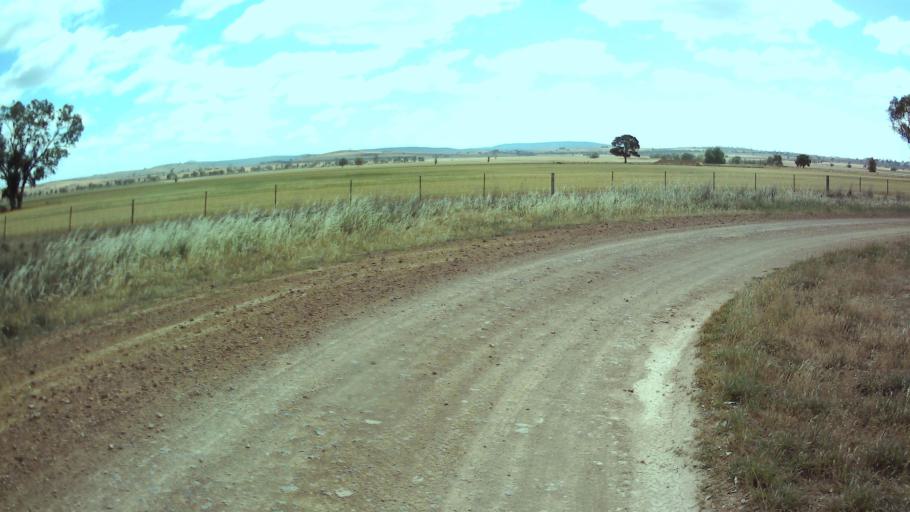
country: AU
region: New South Wales
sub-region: Weddin
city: Grenfell
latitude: -33.9980
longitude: 148.2993
